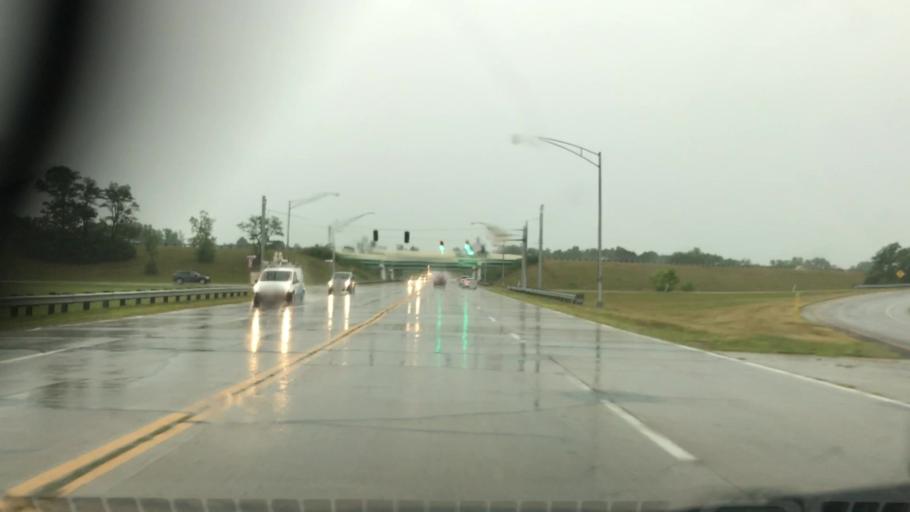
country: US
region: Ohio
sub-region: Greene County
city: Fairborn
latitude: 39.8174
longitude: -84.0030
